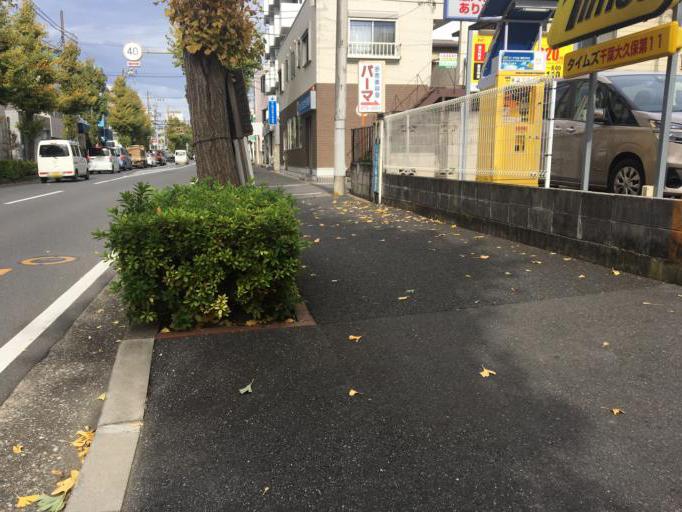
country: JP
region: Chiba
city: Funabashi
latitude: 35.6884
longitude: 140.0508
